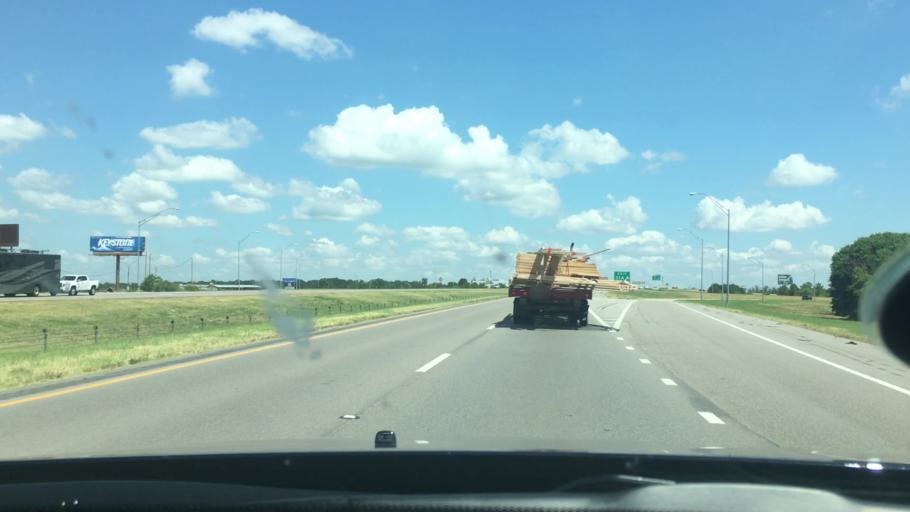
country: US
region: Oklahoma
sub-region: Carter County
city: Ardmore
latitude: 34.1679
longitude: -97.1674
